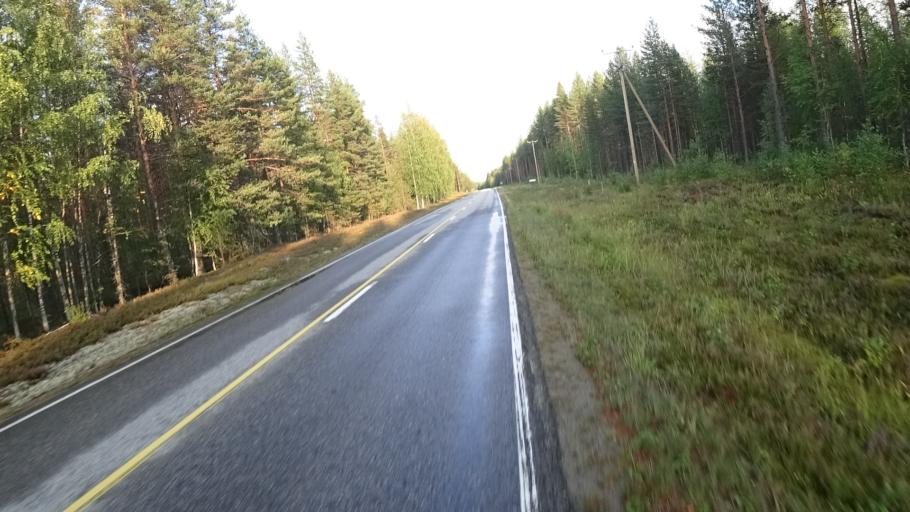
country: FI
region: North Karelia
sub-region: Joensuu
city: Ilomantsi
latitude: 62.6276
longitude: 31.0986
